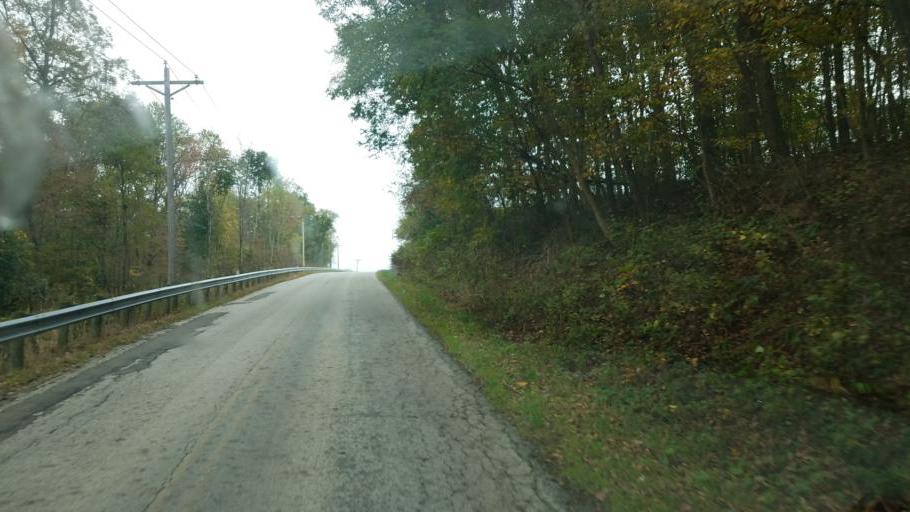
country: US
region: Ohio
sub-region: Ashland County
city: Loudonville
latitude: 40.5752
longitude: -82.1663
